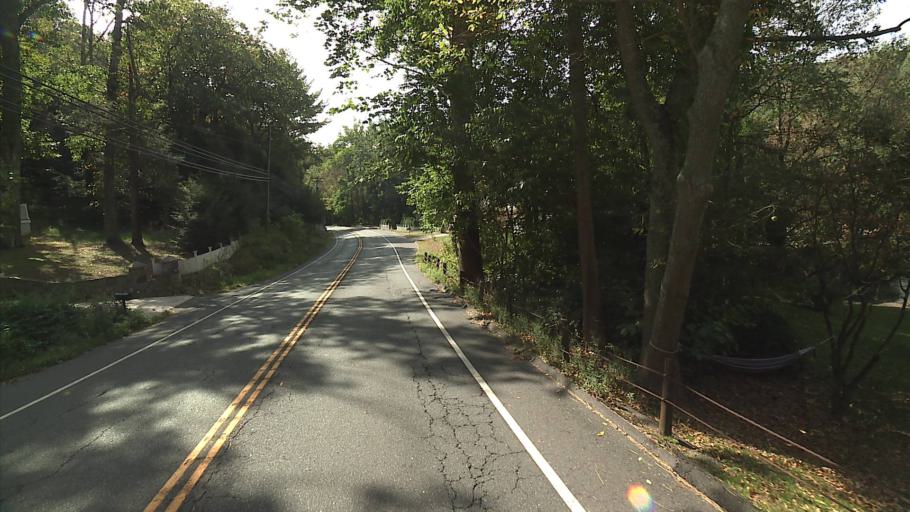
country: US
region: Connecticut
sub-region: New Haven County
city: Oxford
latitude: 41.3810
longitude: -73.1571
